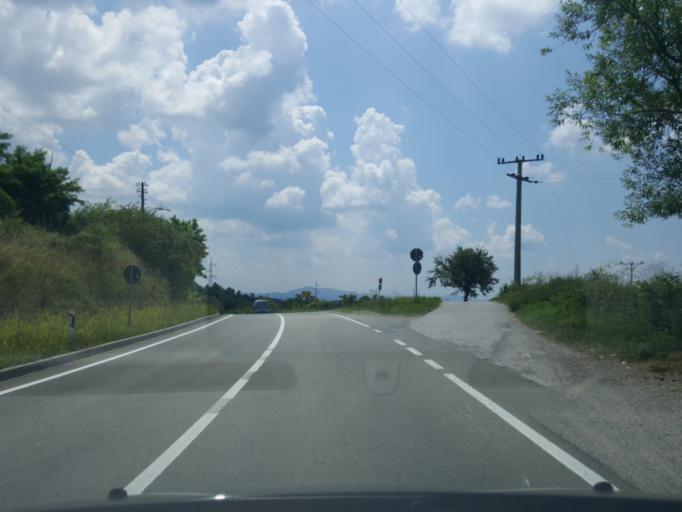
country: RS
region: Central Serbia
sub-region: Moravicki Okrug
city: Gornji Milanovac
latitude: 44.1341
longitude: 20.4936
